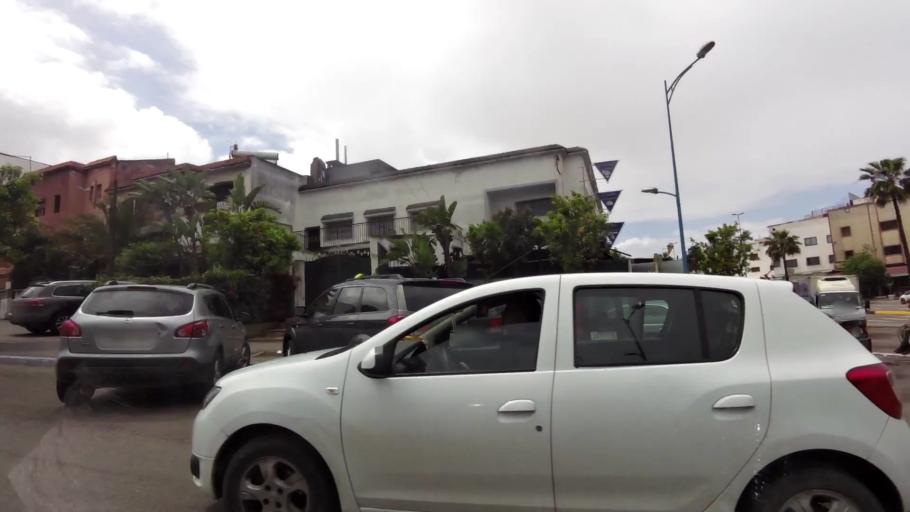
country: MA
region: Grand Casablanca
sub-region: Casablanca
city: Casablanca
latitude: 33.5567
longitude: -7.6822
